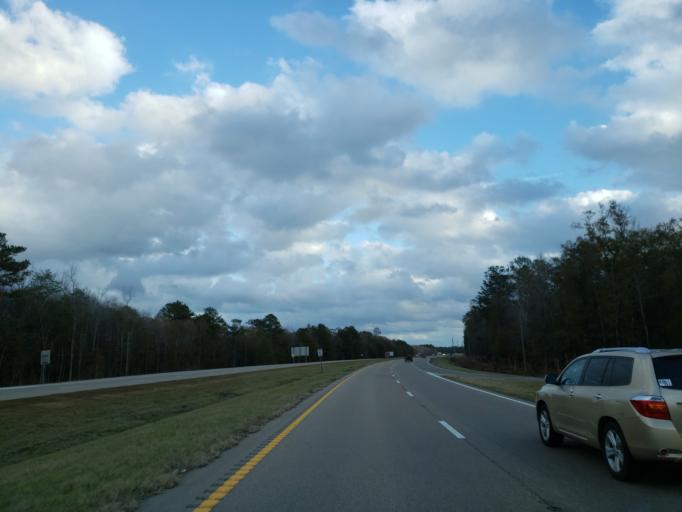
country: US
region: Mississippi
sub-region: Perry County
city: New Augusta
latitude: 31.1518
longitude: -88.8925
